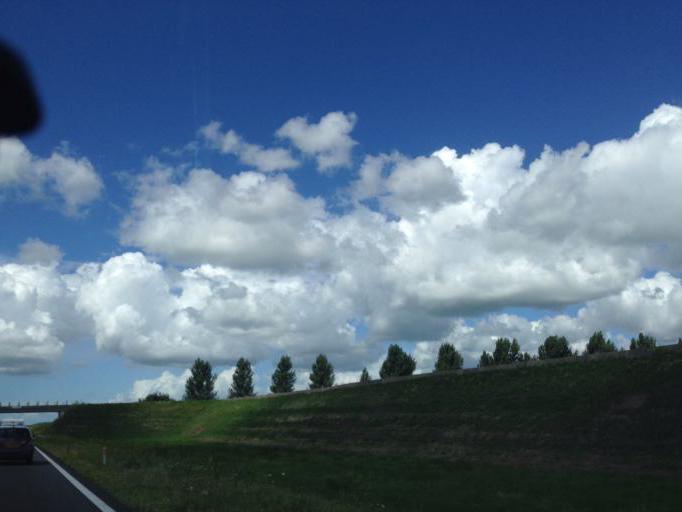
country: NL
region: Overijssel
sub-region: Gemeente Kampen
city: Kampen
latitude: 52.5410
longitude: 5.8997
